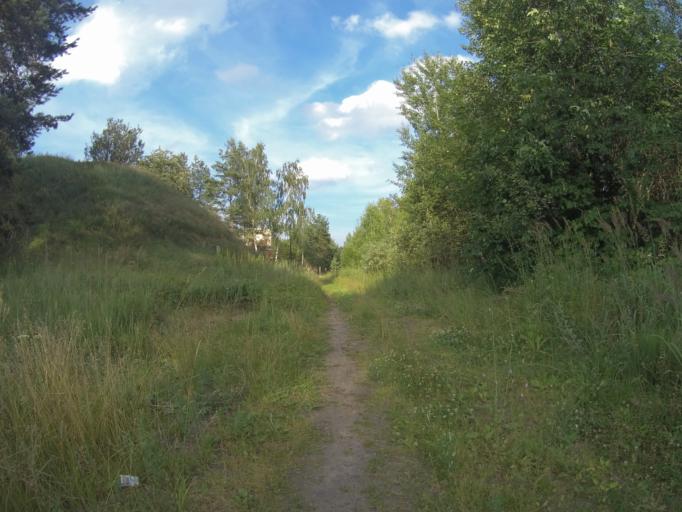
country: RU
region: Vladimir
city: Vorsha
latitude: 56.0020
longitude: 40.0657
